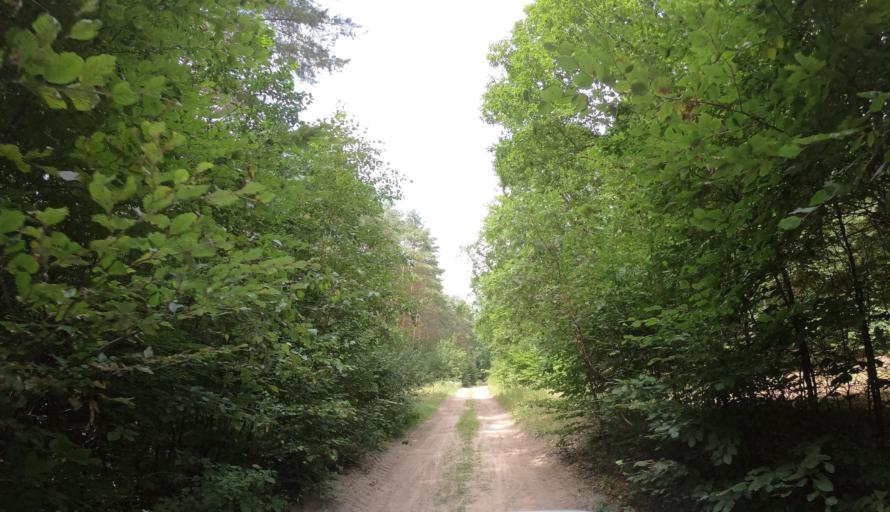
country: PL
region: West Pomeranian Voivodeship
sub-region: Powiat gryfinski
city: Stare Czarnowo
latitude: 53.3345
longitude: 14.8043
